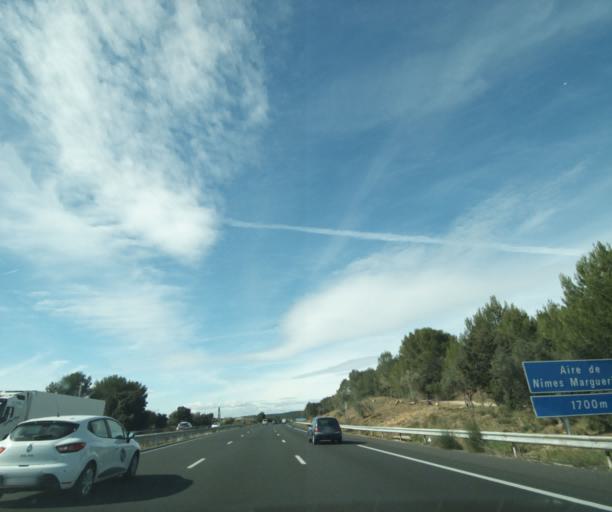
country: FR
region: Languedoc-Roussillon
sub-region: Departement du Gard
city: Saint-Gervasy
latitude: 43.8821
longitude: 4.4756
